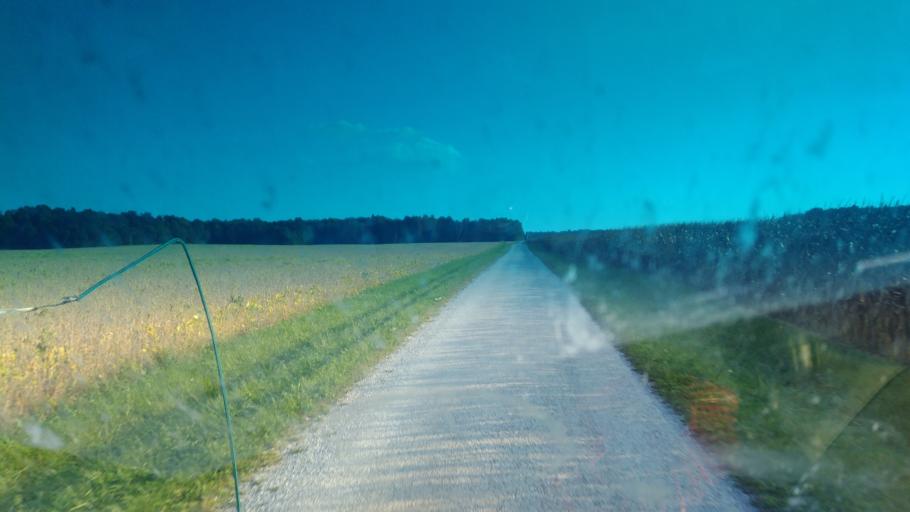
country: US
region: Ohio
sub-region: Crawford County
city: Bucyrus
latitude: 40.9345
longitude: -82.9973
